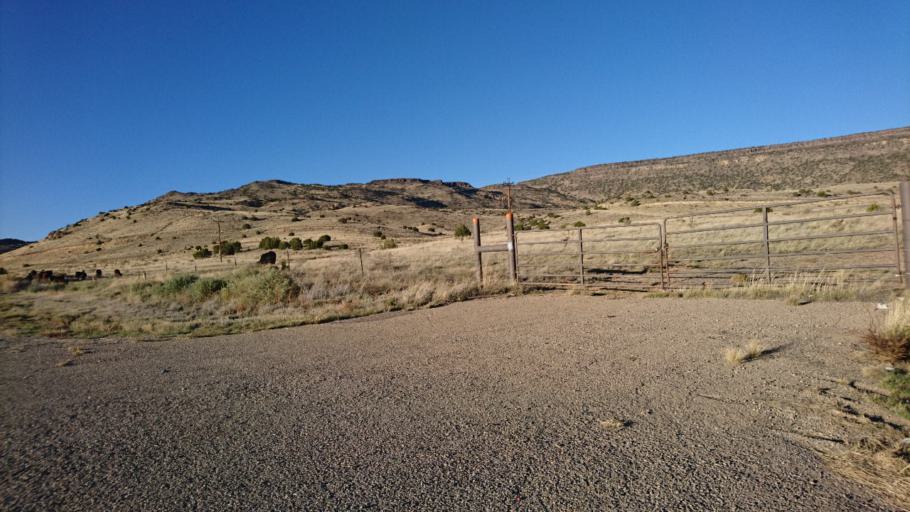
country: US
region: New Mexico
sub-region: Cibola County
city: Grants
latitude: 35.1119
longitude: -107.7824
